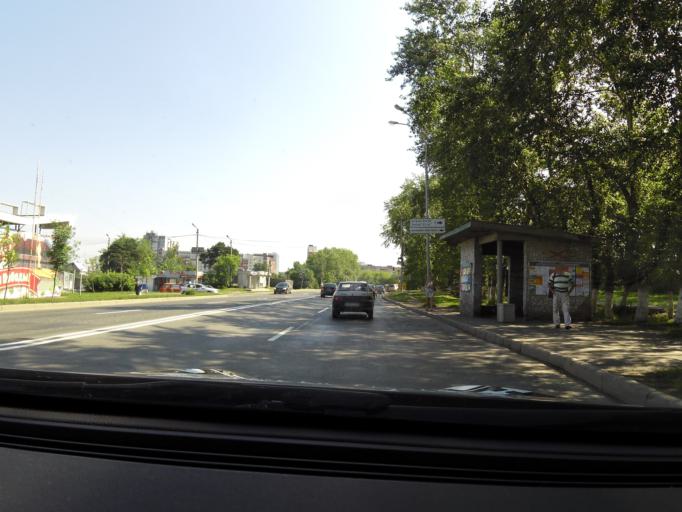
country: RU
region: Sverdlovsk
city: Shirokaya Rechka
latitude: 56.8172
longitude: 60.5316
